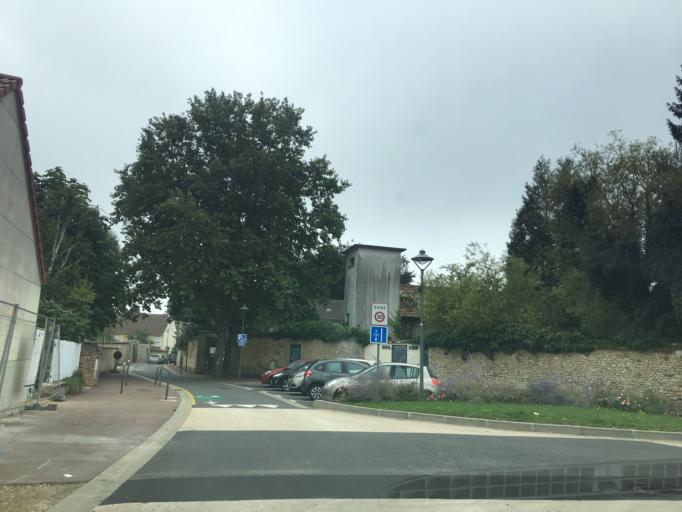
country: FR
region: Ile-de-France
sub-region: Departement de Seine-et-Marne
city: Brie-Comte-Robert
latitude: 48.6945
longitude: 2.6046
